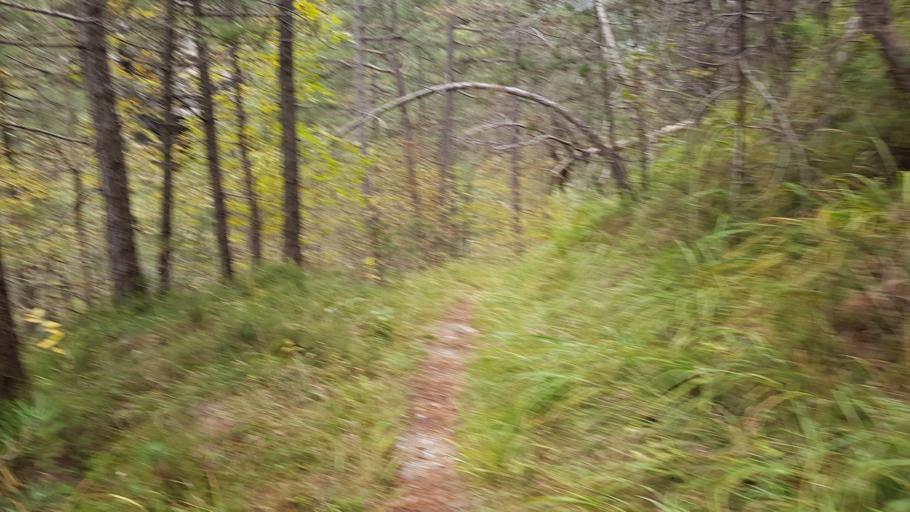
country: IT
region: Friuli Venezia Giulia
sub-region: Provincia di Udine
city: Chiusaforte
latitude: 46.4167
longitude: 13.3282
